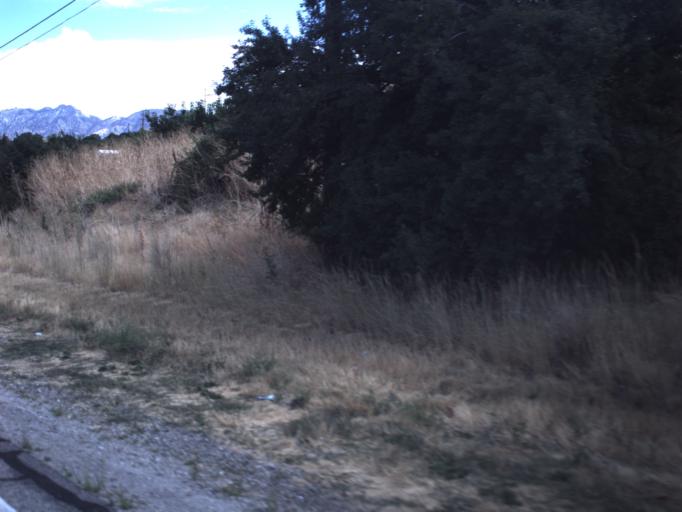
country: US
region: Utah
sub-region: Box Elder County
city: Perry
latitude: 41.4416
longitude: -112.0368
